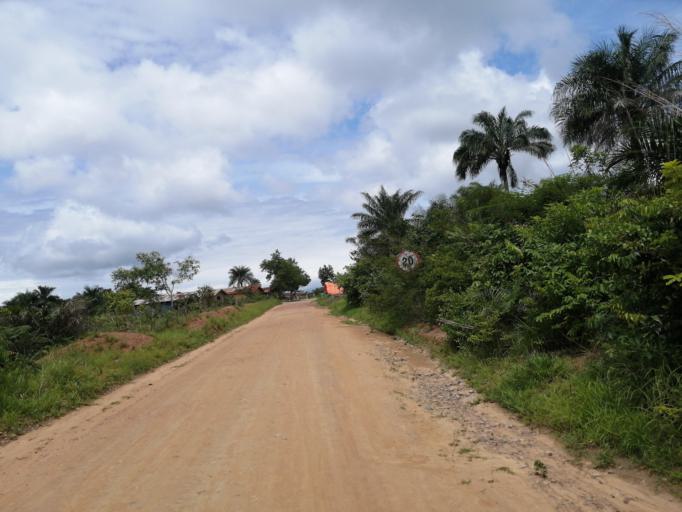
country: SL
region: Northern Province
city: Pepel
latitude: 8.6005
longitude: -13.0547
